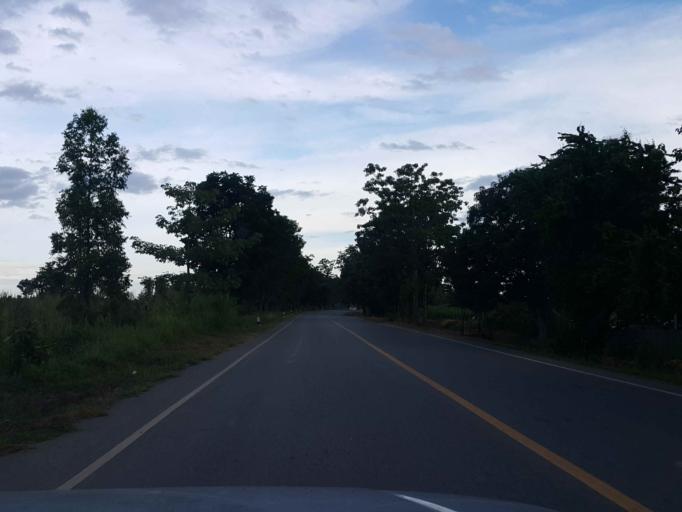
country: TH
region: Sukhothai
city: Sawankhalok
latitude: 17.3728
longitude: 99.7406
